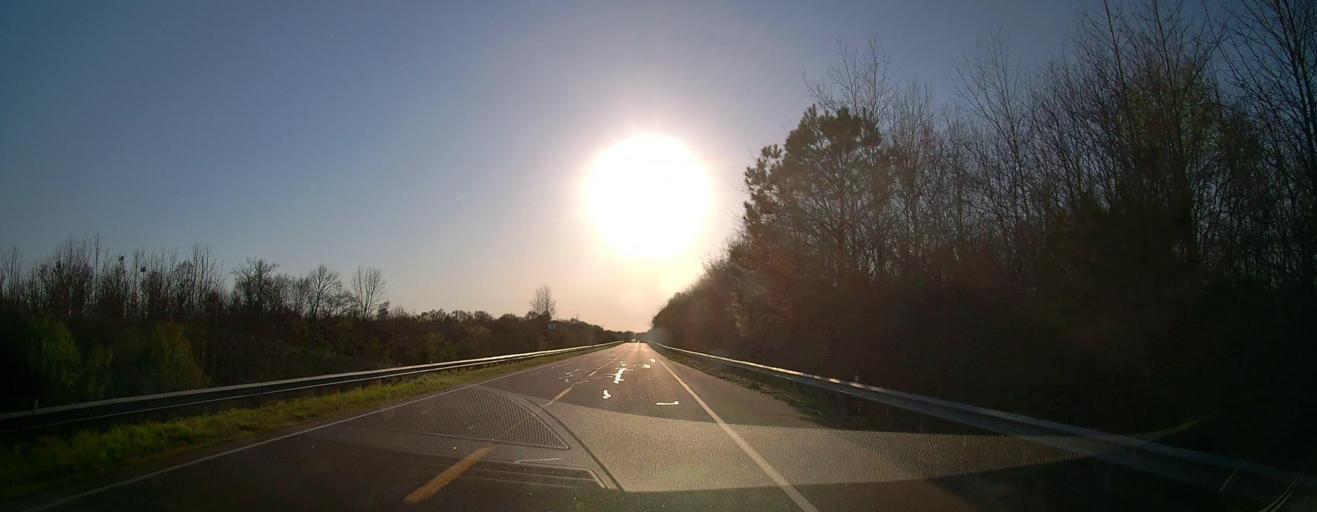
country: US
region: Georgia
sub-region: Wilcox County
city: Abbeville
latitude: 31.9977
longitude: -83.2735
